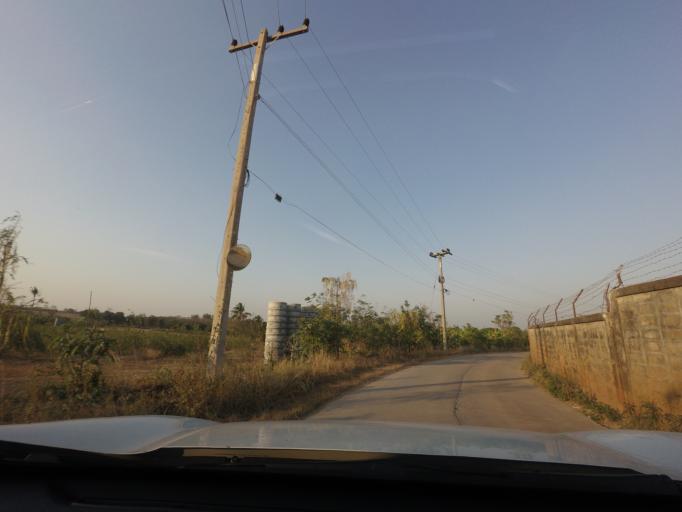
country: TH
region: Nakhon Ratchasima
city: Pak Chong
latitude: 14.6459
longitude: 101.3771
